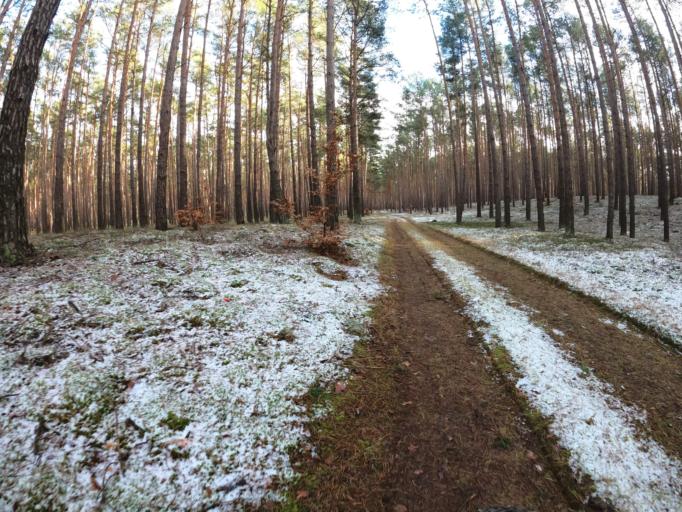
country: PL
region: Lubusz
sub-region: Powiat slubicki
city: Cybinka
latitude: 52.2335
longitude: 14.8295
